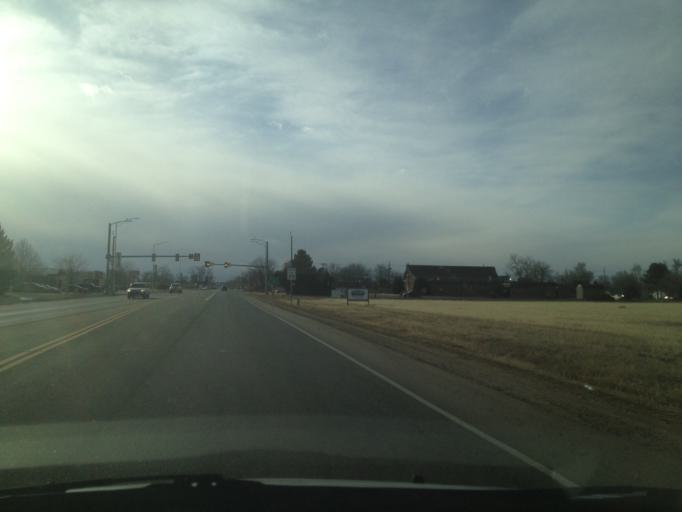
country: US
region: Colorado
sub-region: Weld County
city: Fort Lupton
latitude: 40.0802
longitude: -104.8031
